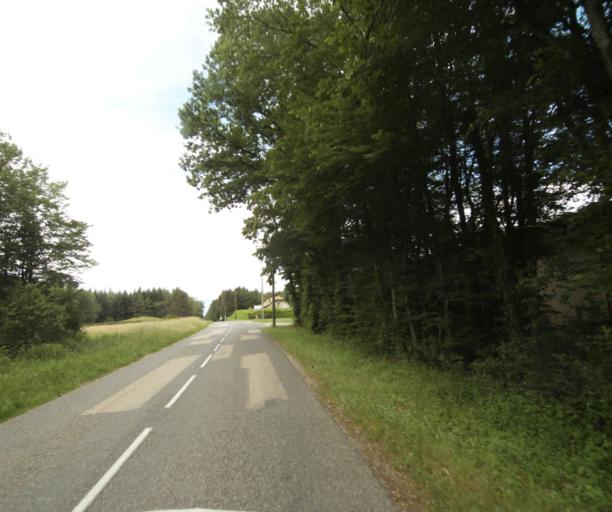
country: FR
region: Rhone-Alpes
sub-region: Departement de la Haute-Savoie
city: Perrignier
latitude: 46.3045
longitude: 6.4124
